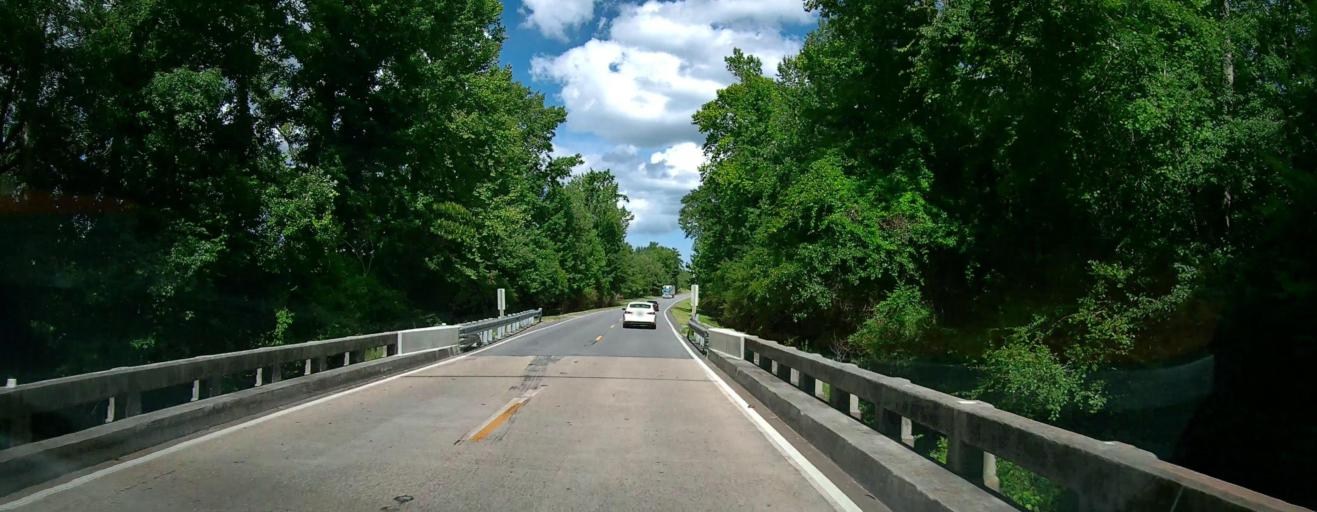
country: US
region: Alabama
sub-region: Lee County
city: Opelika
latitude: 32.4398
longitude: -85.3522
